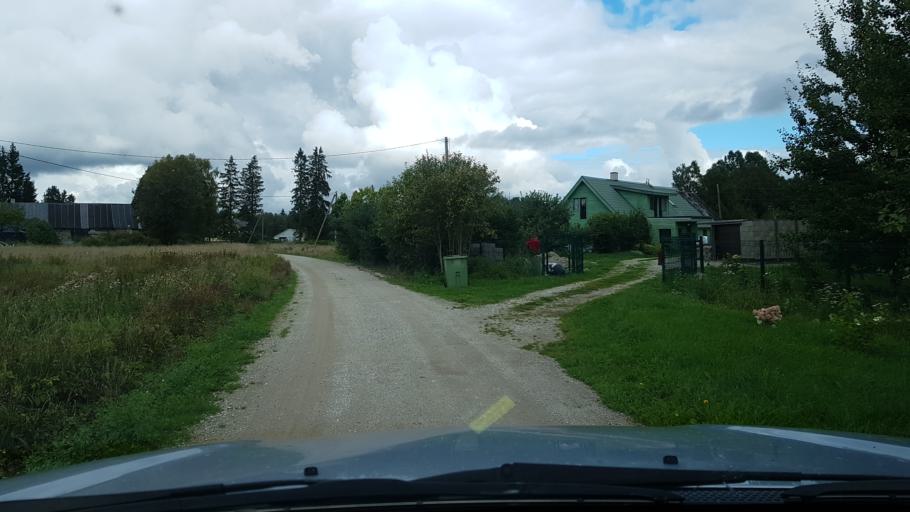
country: EE
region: Harju
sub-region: Raasiku vald
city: Arukula
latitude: 59.2746
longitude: 25.0954
